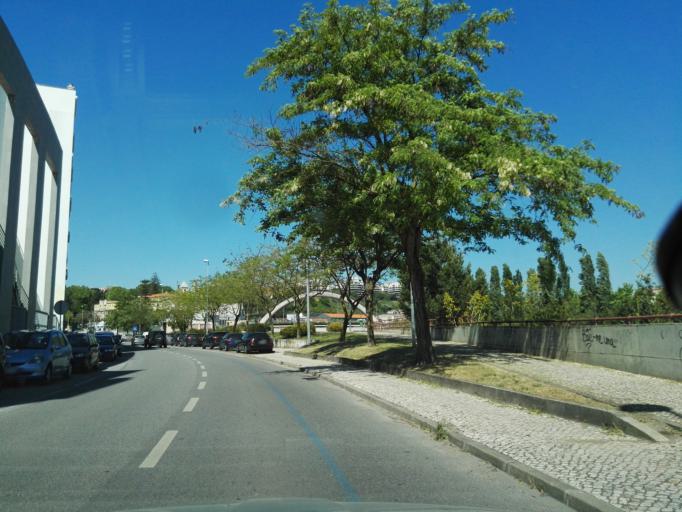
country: PT
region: Lisbon
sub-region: Loures
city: Sacavem
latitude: 38.7970
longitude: -9.1017
